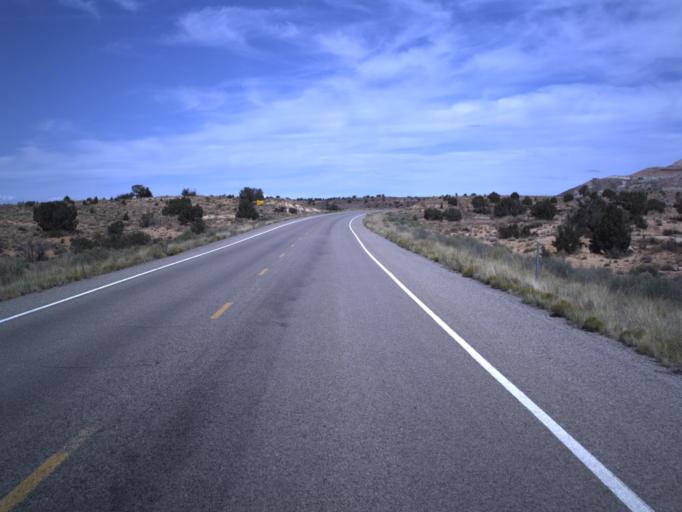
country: US
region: Colorado
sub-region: Montezuma County
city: Towaoc
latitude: 37.1839
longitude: -109.1262
